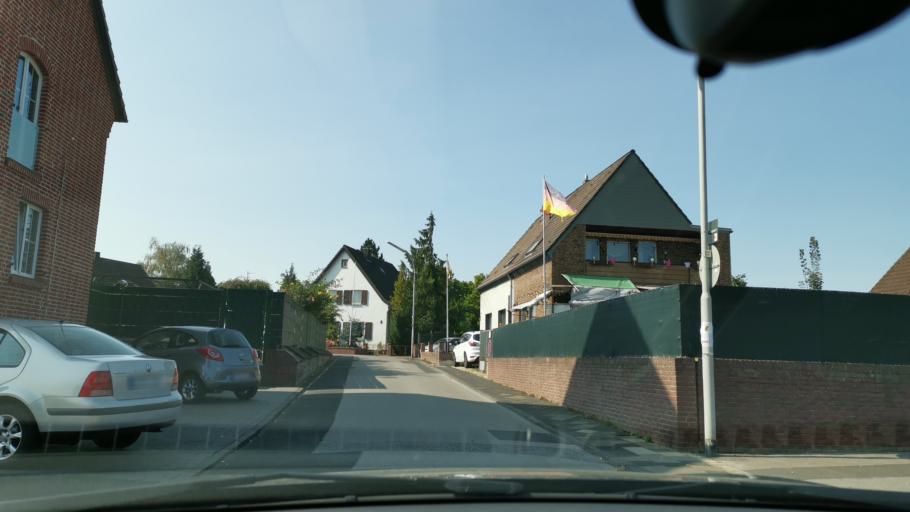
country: DE
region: North Rhine-Westphalia
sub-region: Regierungsbezirk Dusseldorf
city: Grevenbroich
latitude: 51.0707
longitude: 6.5655
